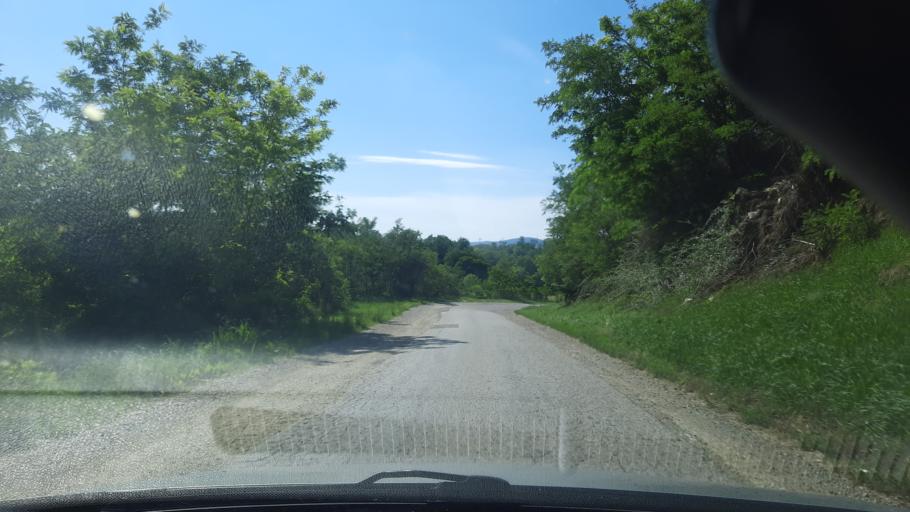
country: RS
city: Cortanovci
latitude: 45.1018
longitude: 19.9905
